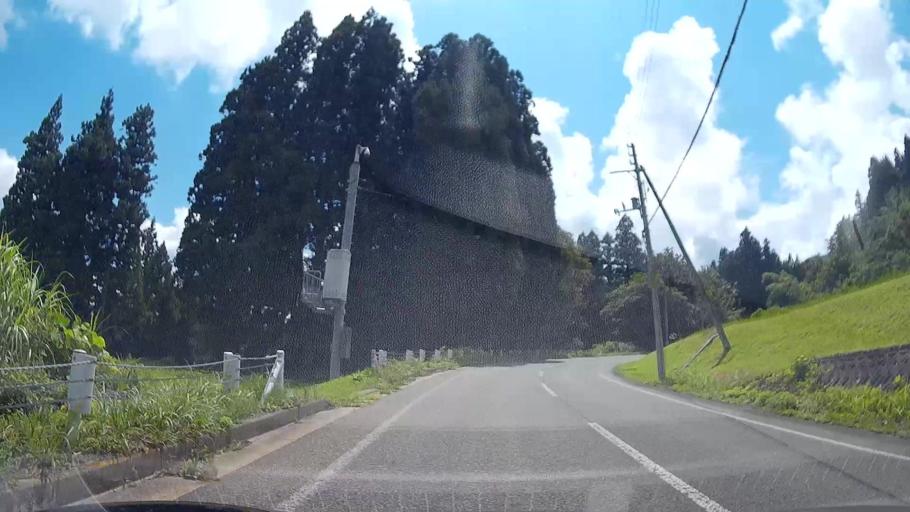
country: JP
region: Niigata
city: Shiozawa
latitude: 37.0239
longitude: 138.8027
